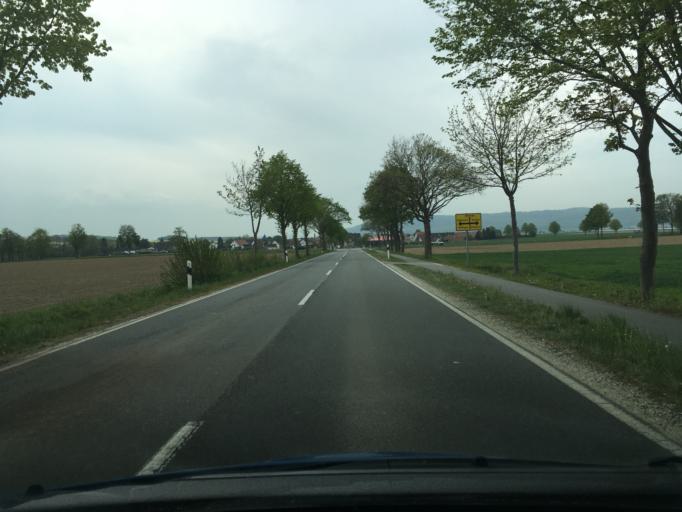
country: DE
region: Lower Saxony
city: Elze
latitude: 52.1707
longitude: 9.7112
